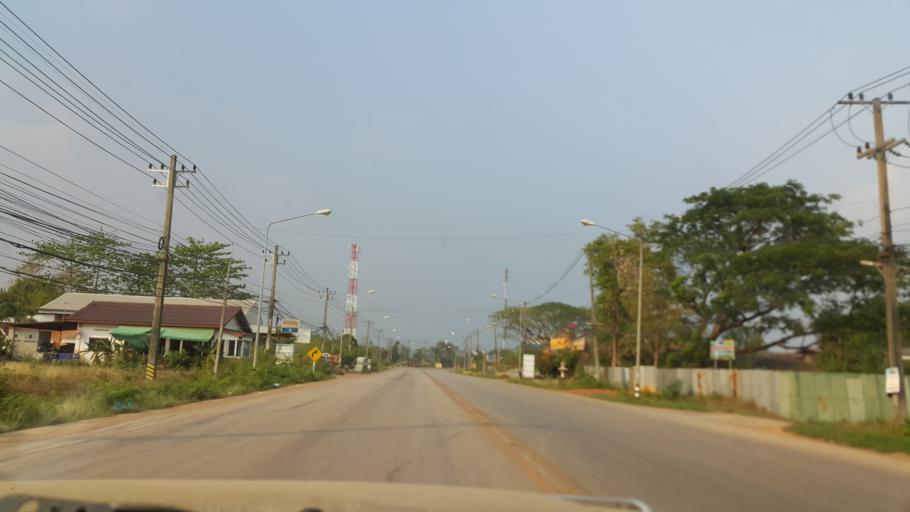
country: TH
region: Nakhon Phanom
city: That Phanom
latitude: 16.9520
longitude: 104.7221
